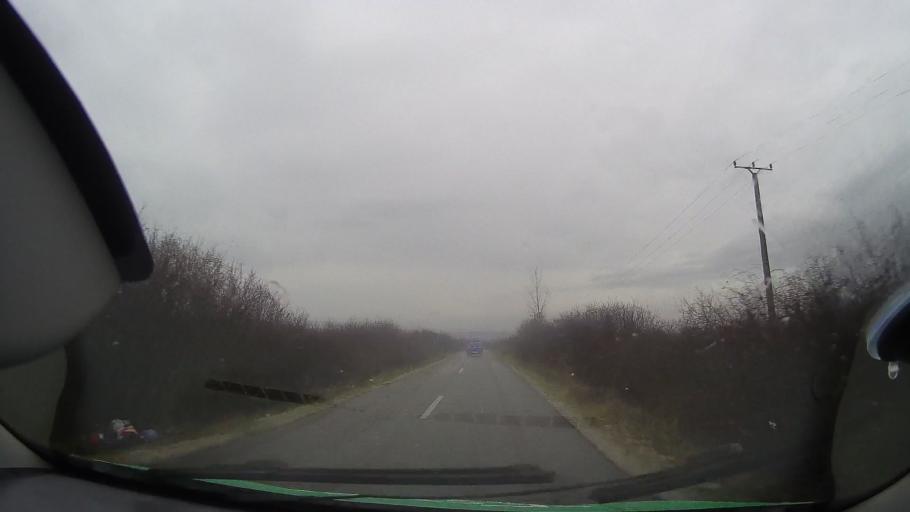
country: RO
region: Bihor
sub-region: Comuna Holod
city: Vintere
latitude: 46.7544
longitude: 22.1476
